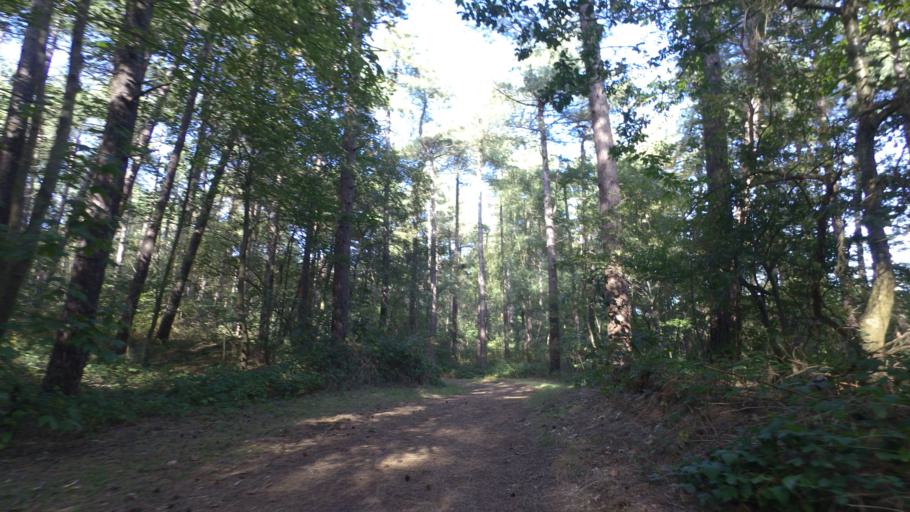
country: NL
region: Friesland
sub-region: Gemeente Ameland
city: Nes
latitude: 53.4515
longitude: 5.7614
